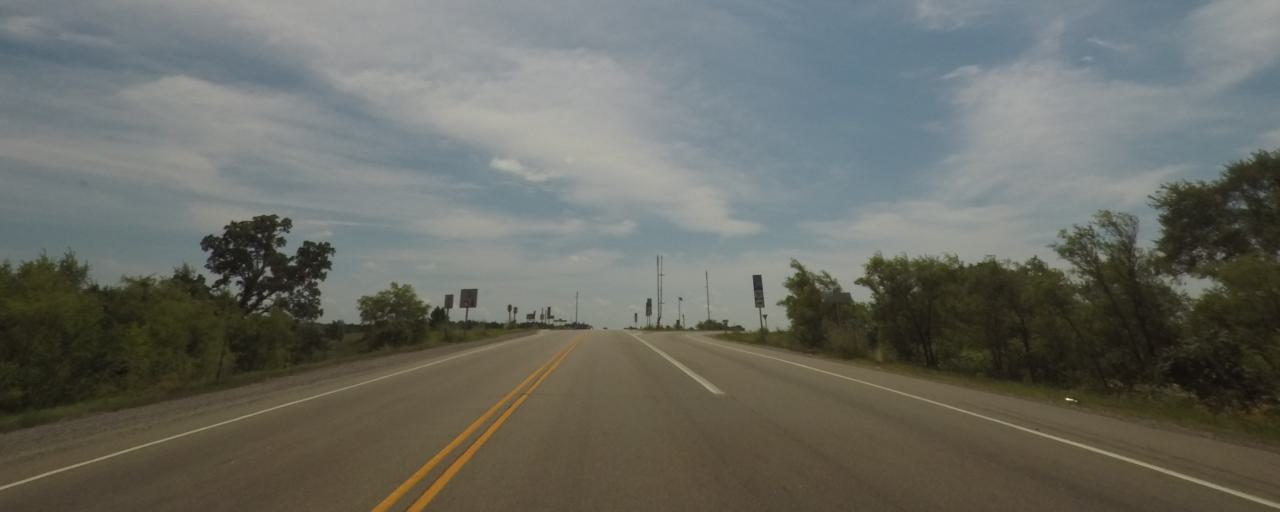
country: US
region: Wisconsin
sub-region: Portage County
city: Plover
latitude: 44.4320
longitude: -89.5207
